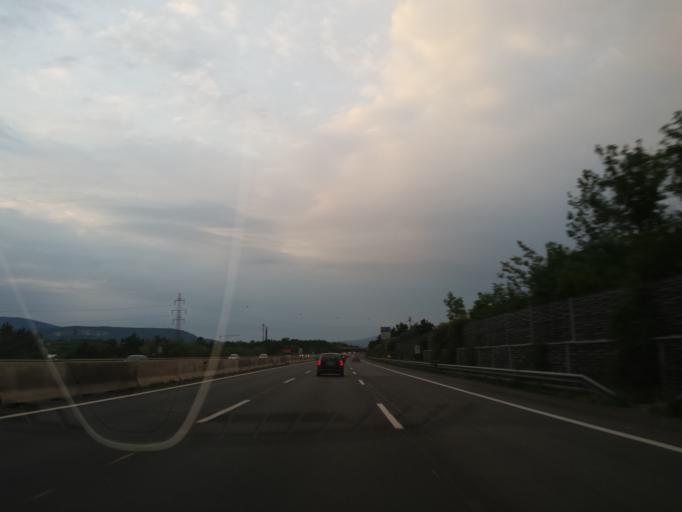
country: AT
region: Lower Austria
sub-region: Politischer Bezirk Baden
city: Leobersdorf
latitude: 47.9277
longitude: 16.2093
